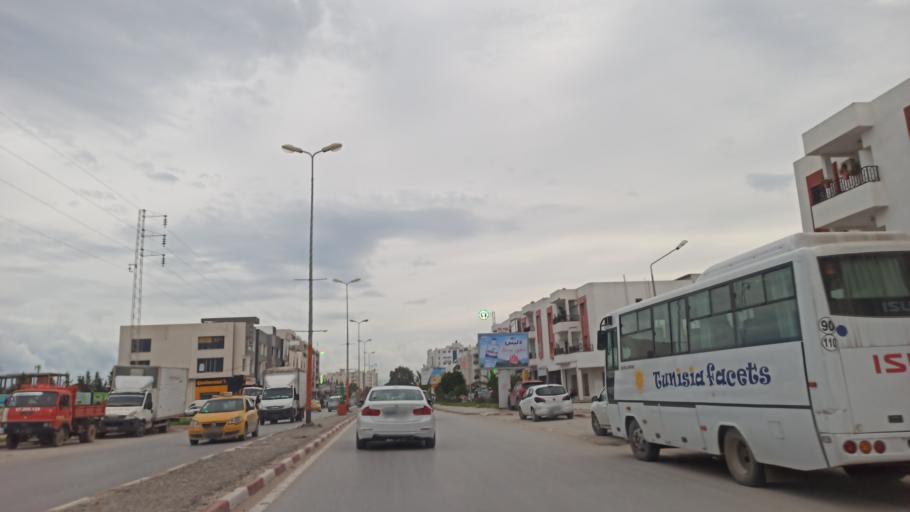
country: TN
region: Ariana
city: Ariana
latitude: 36.8649
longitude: 10.2523
